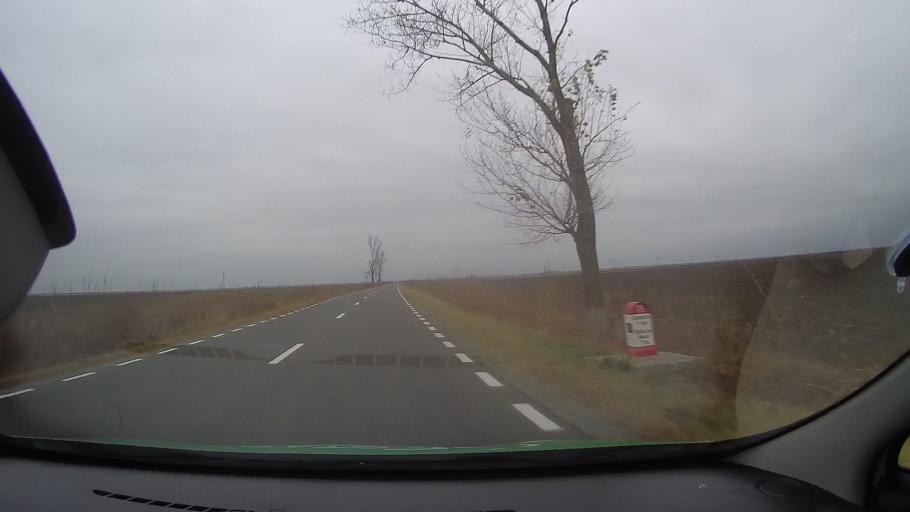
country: RO
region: Ialomita
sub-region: Comuna Gheorghe Lazar
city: Gheorghe Lazar
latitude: 44.6580
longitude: 27.4117
